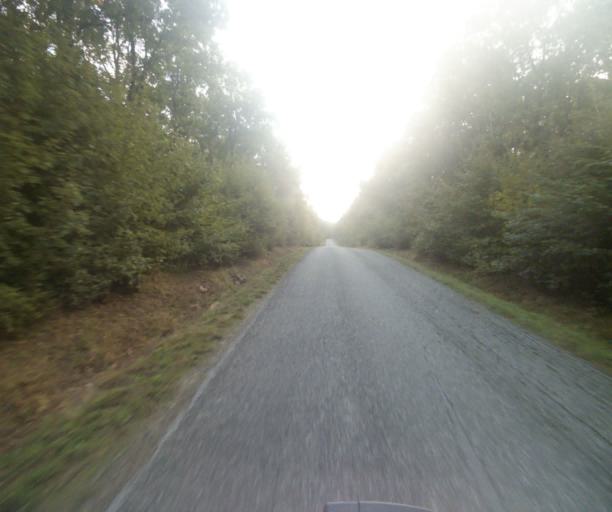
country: FR
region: Midi-Pyrenees
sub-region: Departement du Tarn-et-Garonne
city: Montech
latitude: 43.9385
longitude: 1.2666
